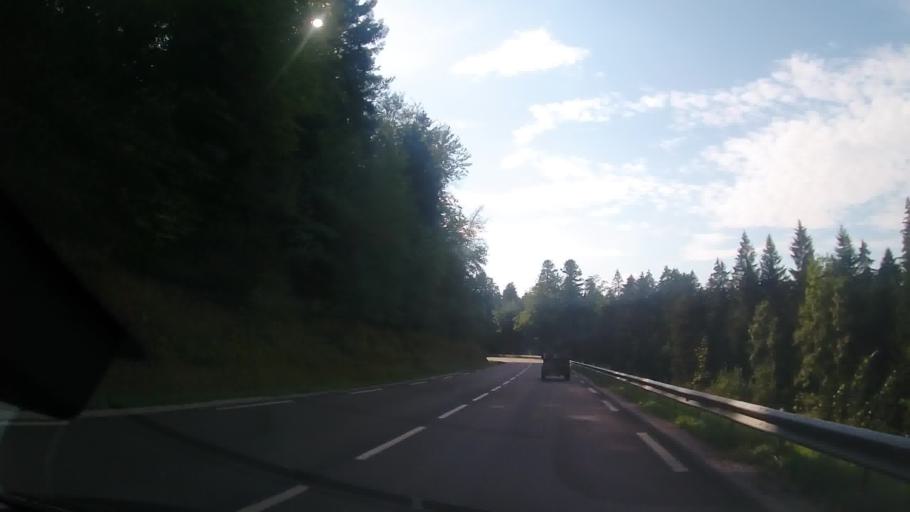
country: FR
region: Franche-Comte
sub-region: Departement du Jura
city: Clairvaux-les-Lacs
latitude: 46.6065
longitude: 5.8837
